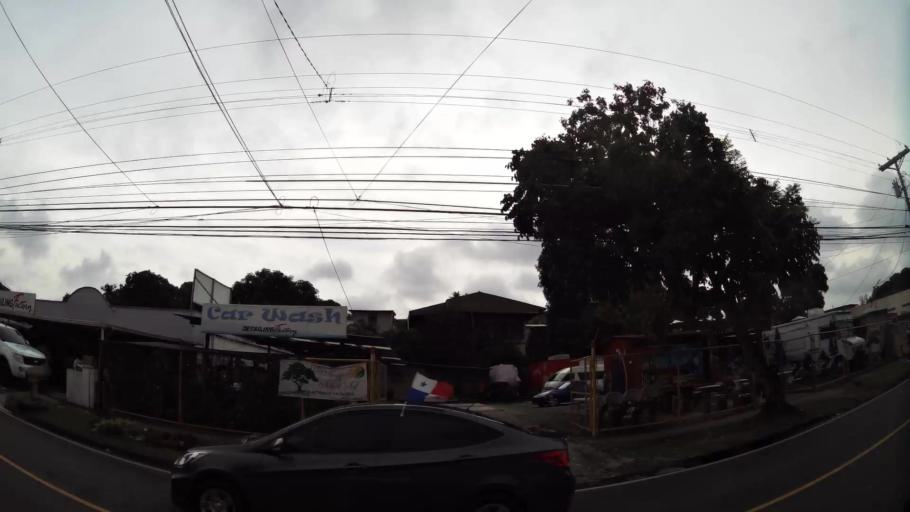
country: PA
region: Panama
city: Panama
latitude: 9.0117
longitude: -79.5309
